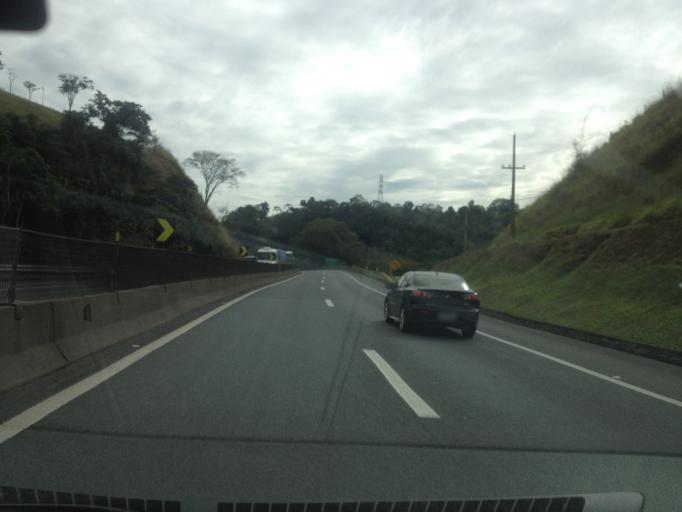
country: BR
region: Rio de Janeiro
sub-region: Pirai
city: Pirai
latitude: -22.6407
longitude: -43.8984
